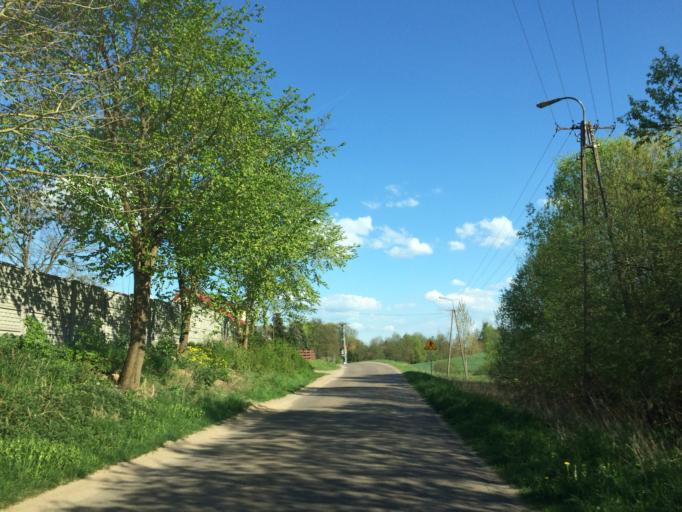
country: PL
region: Warmian-Masurian Voivodeship
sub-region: Powiat dzialdowski
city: Rybno
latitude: 53.4212
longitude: 19.9255
